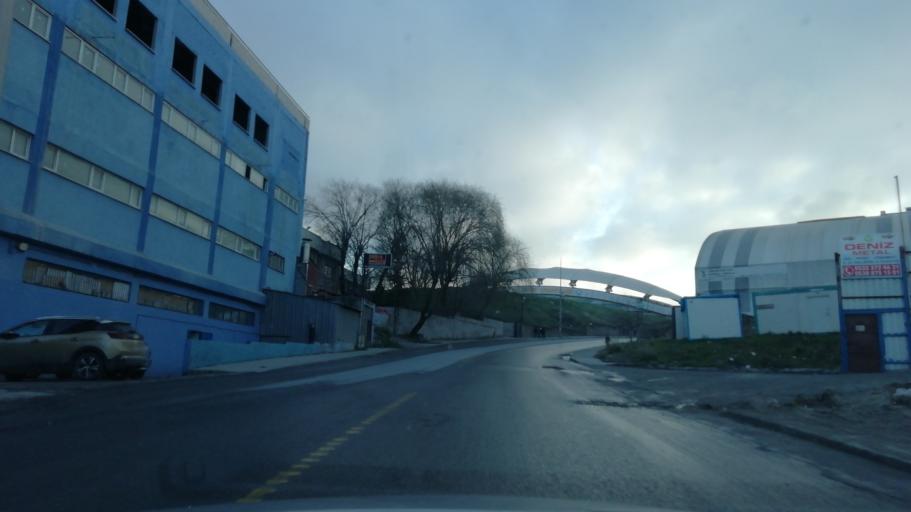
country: TR
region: Istanbul
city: Esenyurt
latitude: 41.0161
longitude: 28.7004
